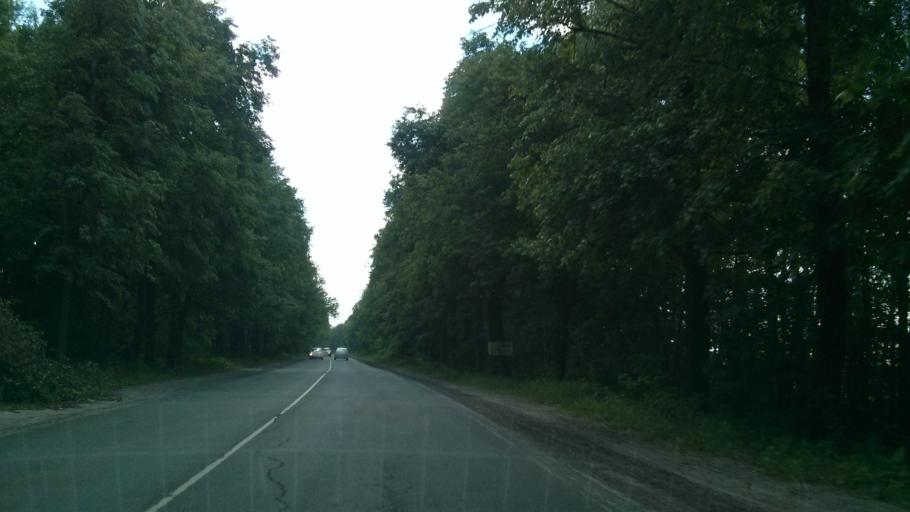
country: RU
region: Vladimir
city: Murom
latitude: 55.5449
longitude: 41.9888
